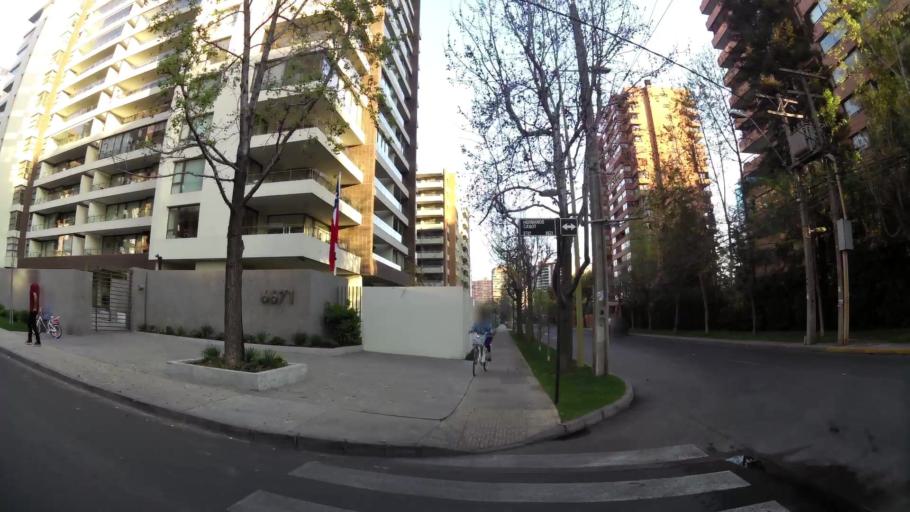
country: CL
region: Santiago Metropolitan
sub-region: Provincia de Santiago
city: Villa Presidente Frei, Nunoa, Santiago, Chile
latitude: -33.3968
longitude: -70.5649
